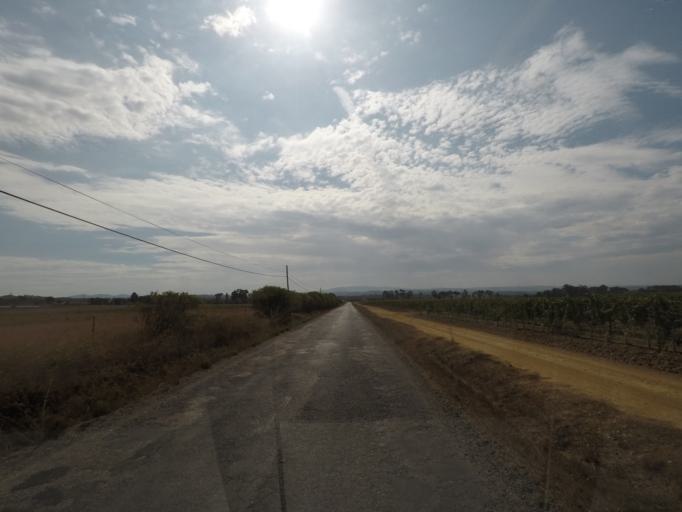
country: PT
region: Beja
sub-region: Odemira
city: Sao Teotonio
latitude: 37.4707
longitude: -8.7547
